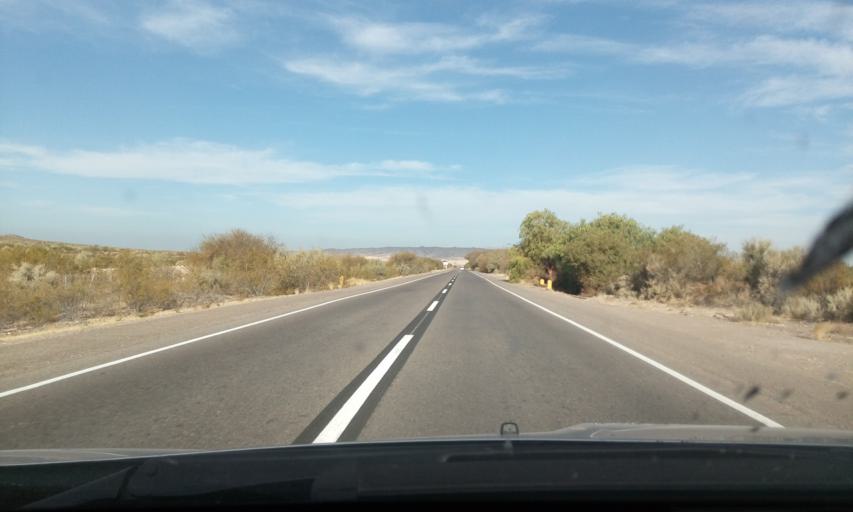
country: AR
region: San Juan
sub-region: Departamento de Rivadavia
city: Rivadavia
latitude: -31.4293
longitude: -68.6679
